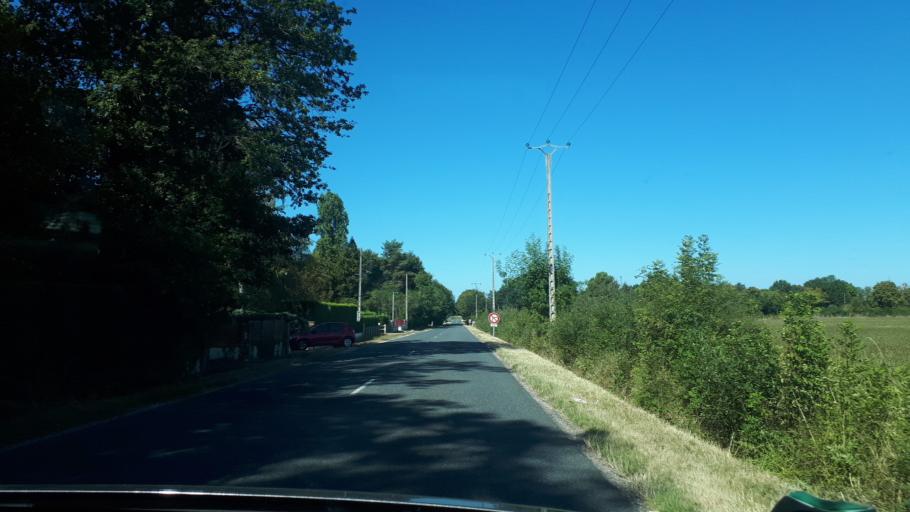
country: FR
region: Centre
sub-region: Departement du Loiret
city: Coullons
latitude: 47.6193
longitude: 2.5221
